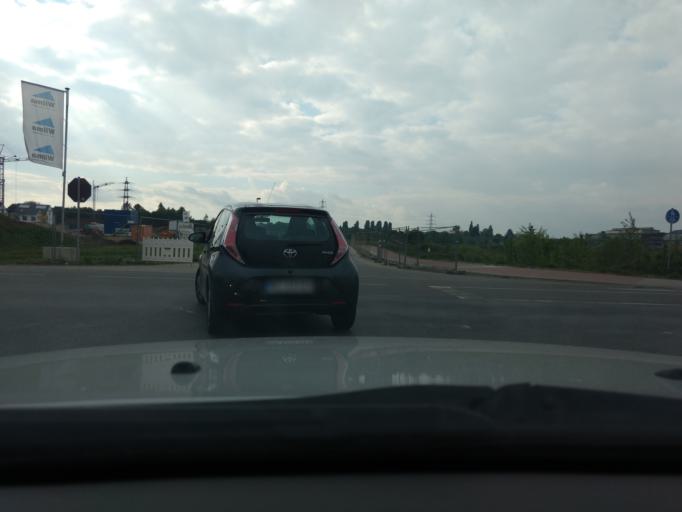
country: DE
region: North Rhine-Westphalia
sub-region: Regierungsbezirk Dusseldorf
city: Meerbusch
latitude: 51.2414
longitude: 6.7117
